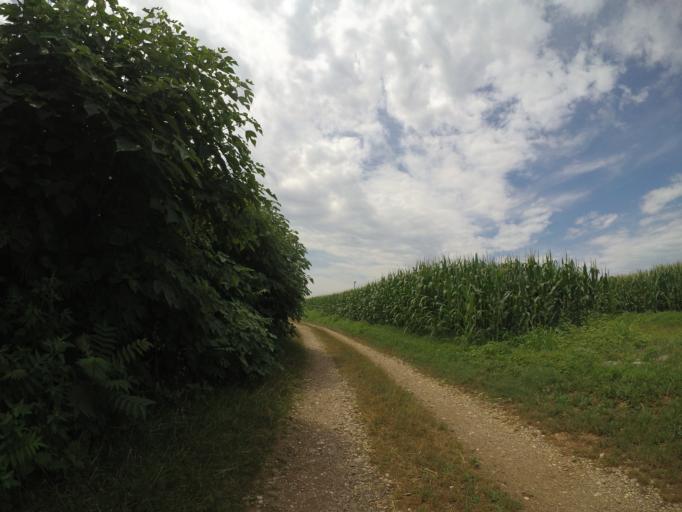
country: IT
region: Friuli Venezia Giulia
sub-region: Provincia di Udine
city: Bertiolo
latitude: 45.9702
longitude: 13.0569
